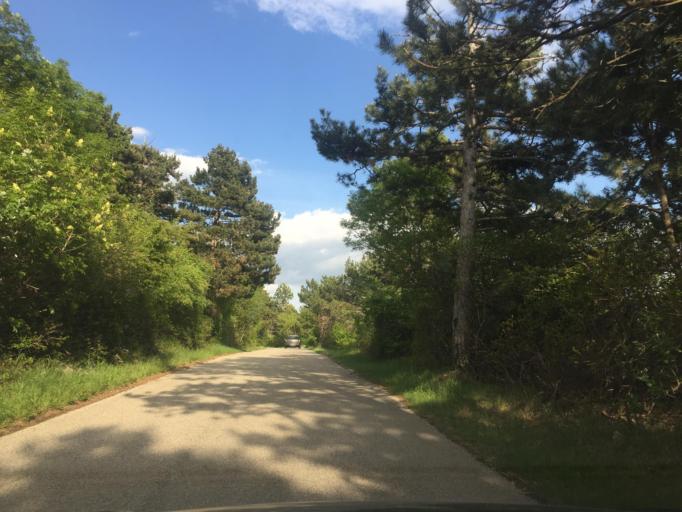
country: IT
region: Friuli Venezia Giulia
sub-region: Provincia di Trieste
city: Dolina
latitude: 45.6283
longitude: 13.8753
